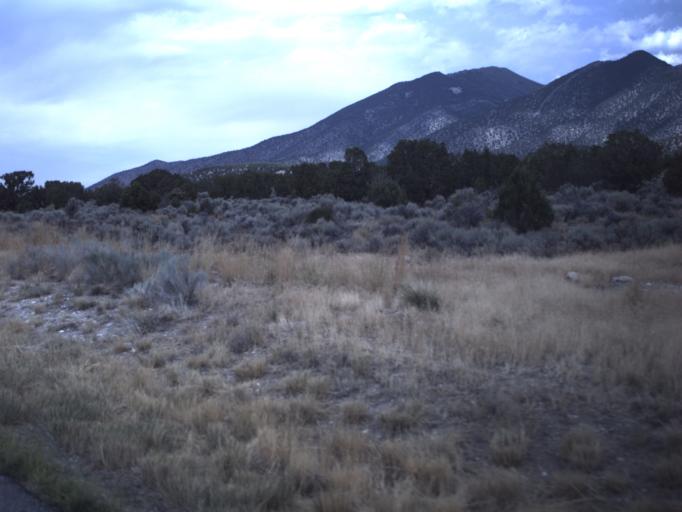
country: US
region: Utah
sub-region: Tooele County
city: Tooele
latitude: 40.3338
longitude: -112.2976
